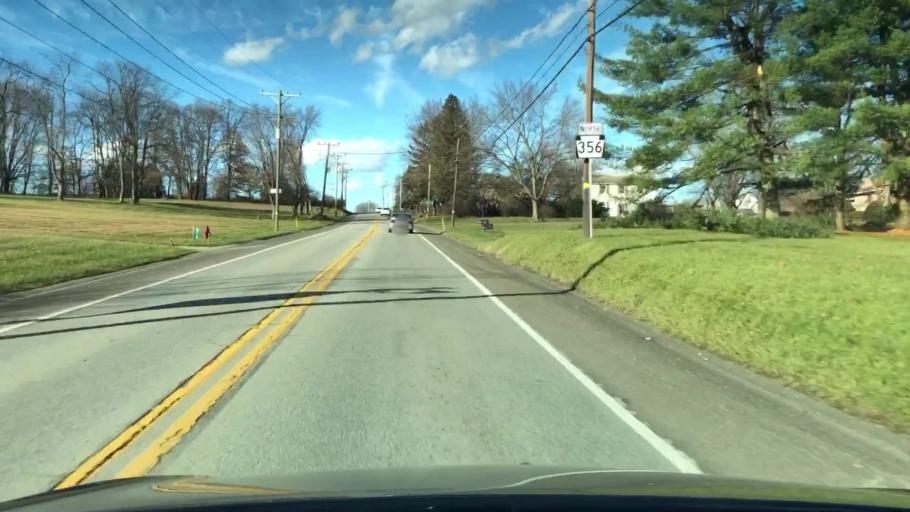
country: US
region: Pennsylvania
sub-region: Butler County
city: Saxonburg
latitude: 40.7259
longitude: -79.7571
